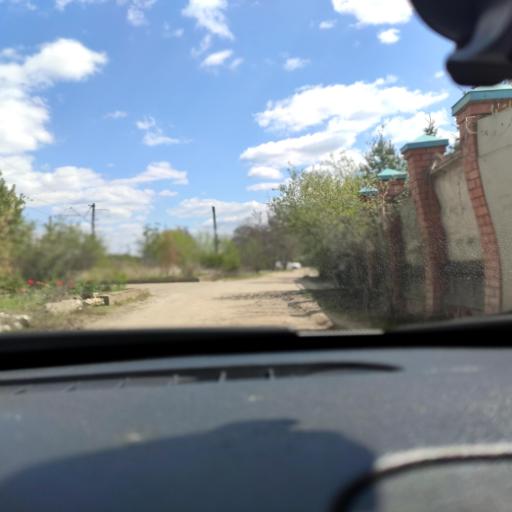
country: RU
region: Voronezj
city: Voronezh
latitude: 51.7213
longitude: 39.2442
